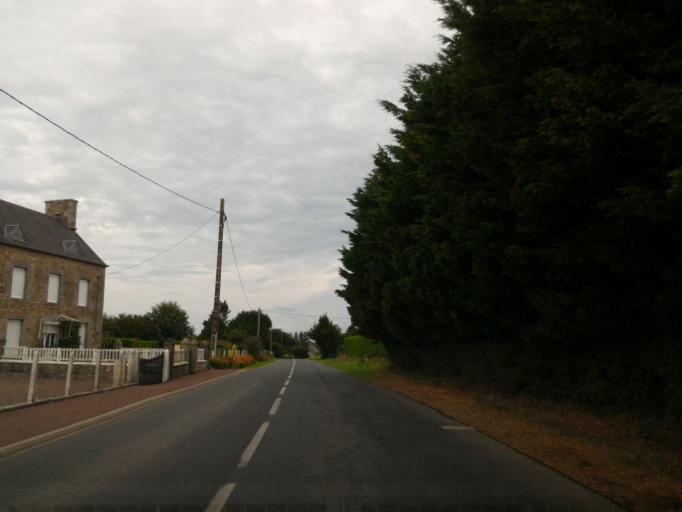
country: FR
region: Lower Normandy
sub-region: Departement de la Manche
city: La Haye-Pesnel
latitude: 48.7853
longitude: -1.4194
